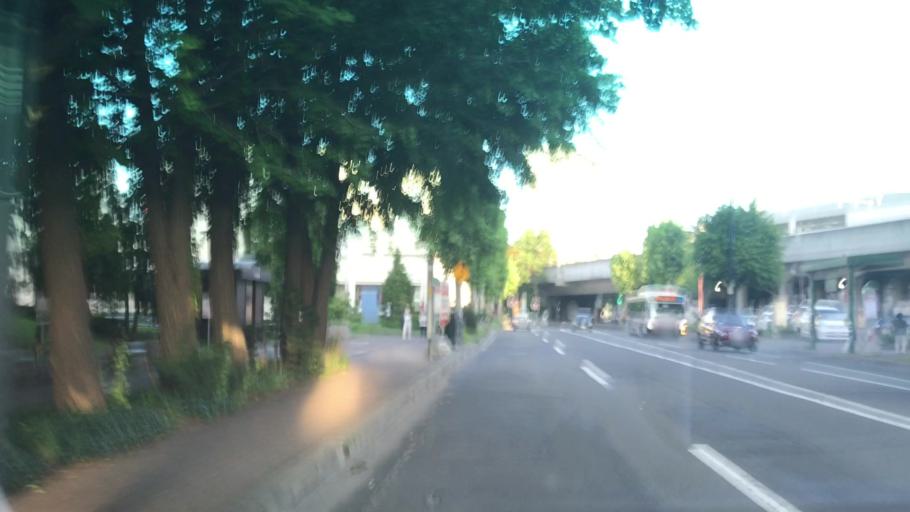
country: JP
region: Hokkaido
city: Sapporo
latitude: 43.0708
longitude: 141.3333
